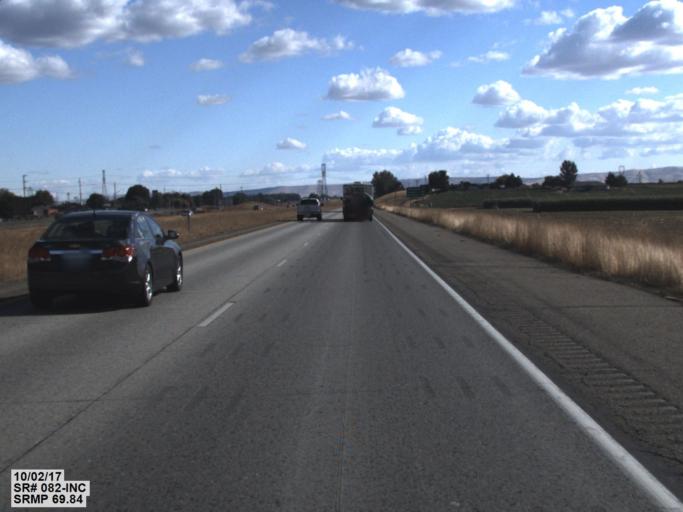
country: US
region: Washington
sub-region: Yakima County
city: Sunnyside
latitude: 46.2999
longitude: -119.9636
